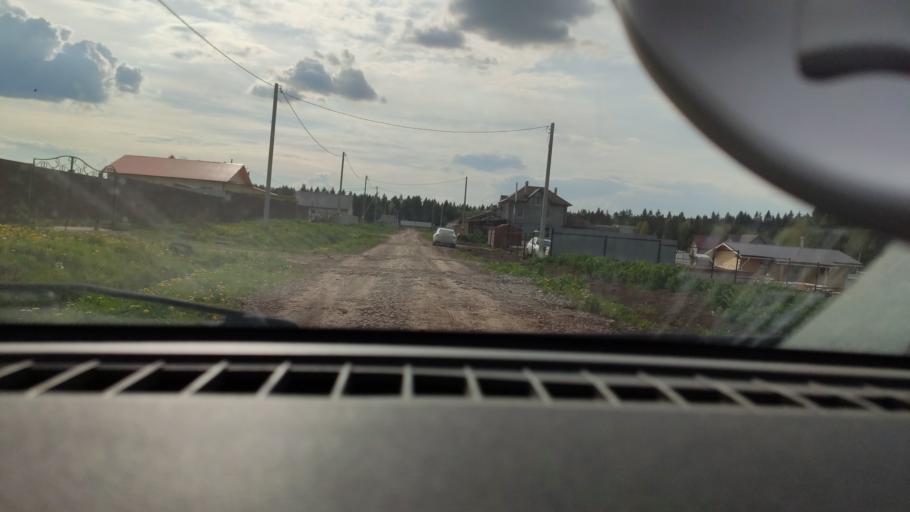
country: RU
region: Perm
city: Ferma
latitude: 57.9491
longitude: 56.3357
